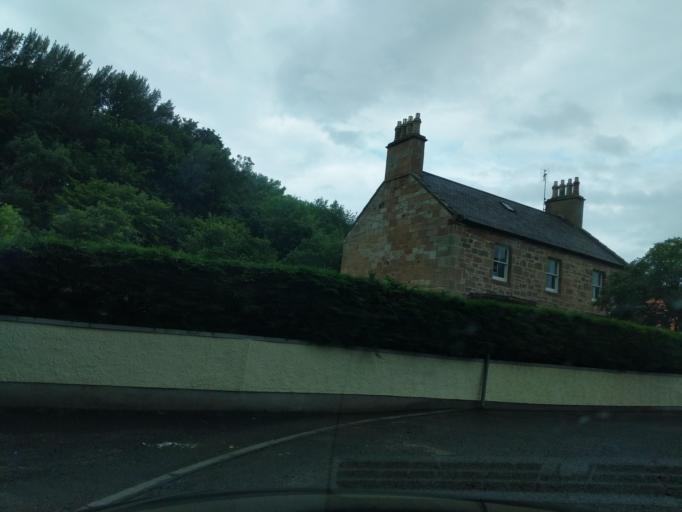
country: GB
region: Scotland
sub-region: Midlothian
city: Dalkeith
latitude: 55.8946
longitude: -3.0780
